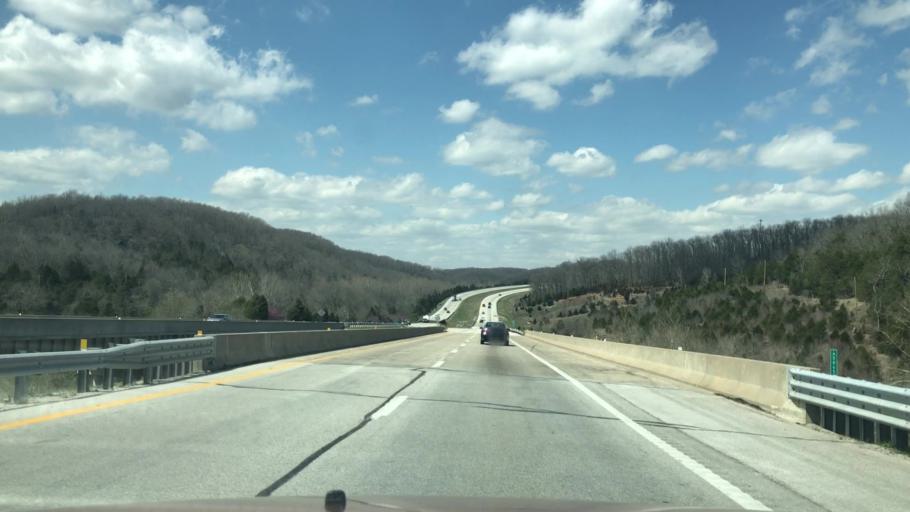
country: US
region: Missouri
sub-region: Christian County
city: Ozark
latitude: 36.9054
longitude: -93.2423
